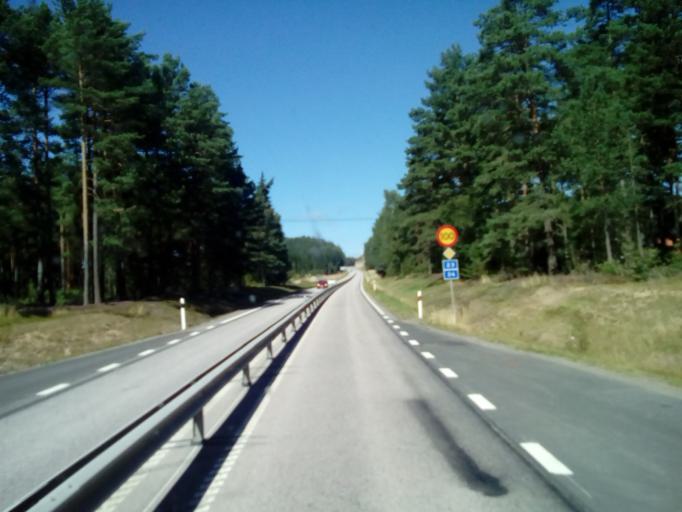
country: SE
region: OEstergoetland
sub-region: Kinda Kommun
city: Rimforsa
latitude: 58.0740
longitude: 15.6536
